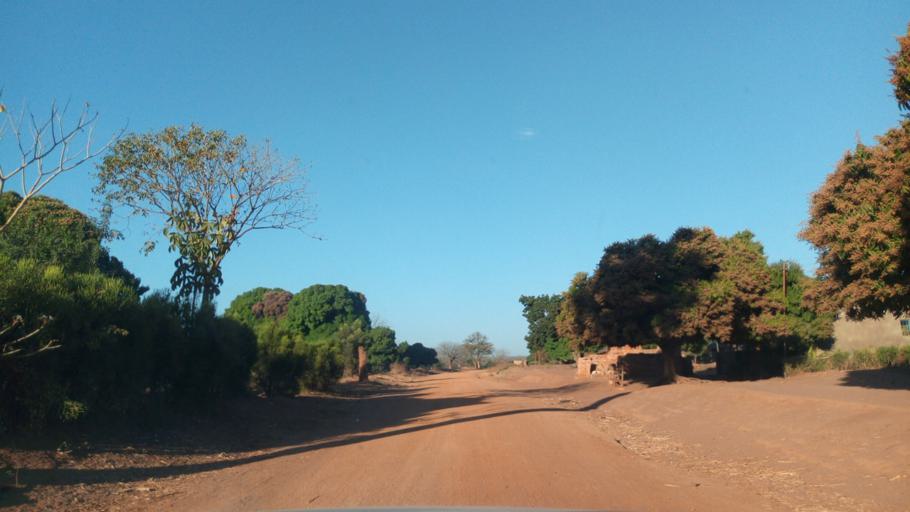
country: ZM
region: Luapula
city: Mwense
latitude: -10.4047
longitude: 28.6171
